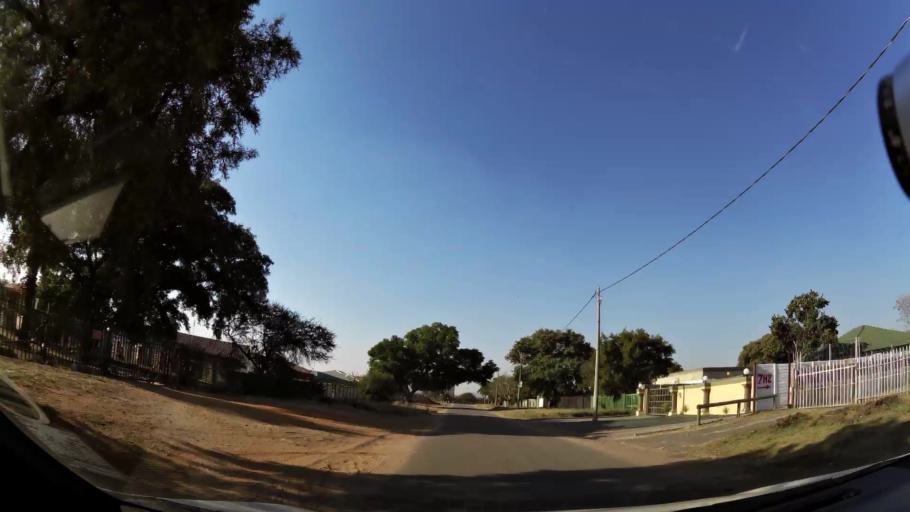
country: ZA
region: North-West
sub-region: Bojanala Platinum District Municipality
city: Rustenburg
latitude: -25.6545
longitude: 27.2600
